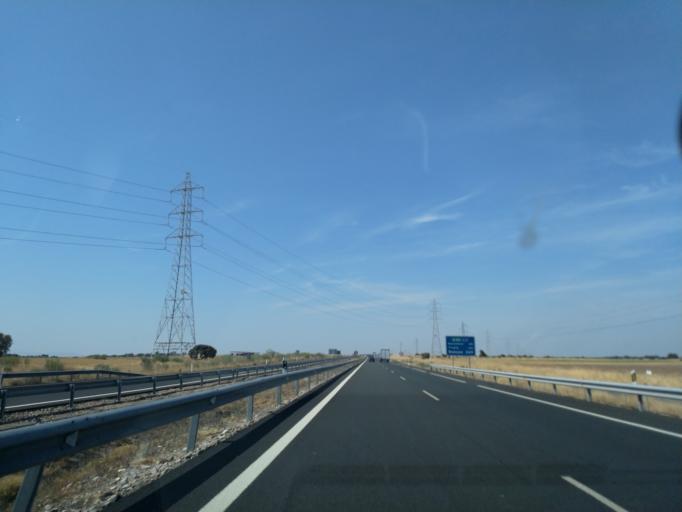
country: ES
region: Castille-La Mancha
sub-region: Province of Toledo
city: Velada
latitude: 39.9356
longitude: -4.9851
